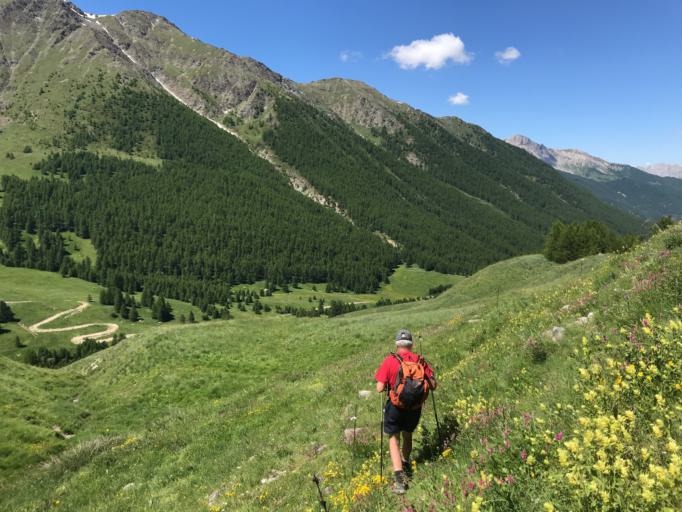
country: IT
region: Piedmont
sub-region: Provincia di Cuneo
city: Pontechianale
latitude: 44.7197
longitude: 6.9162
